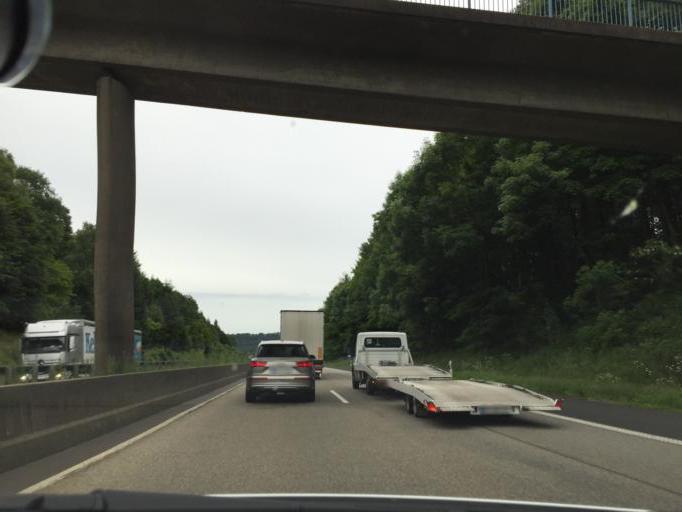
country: DE
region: Bavaria
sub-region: Regierungsbezirk Unterfranken
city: Motten
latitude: 50.3668
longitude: 9.7326
